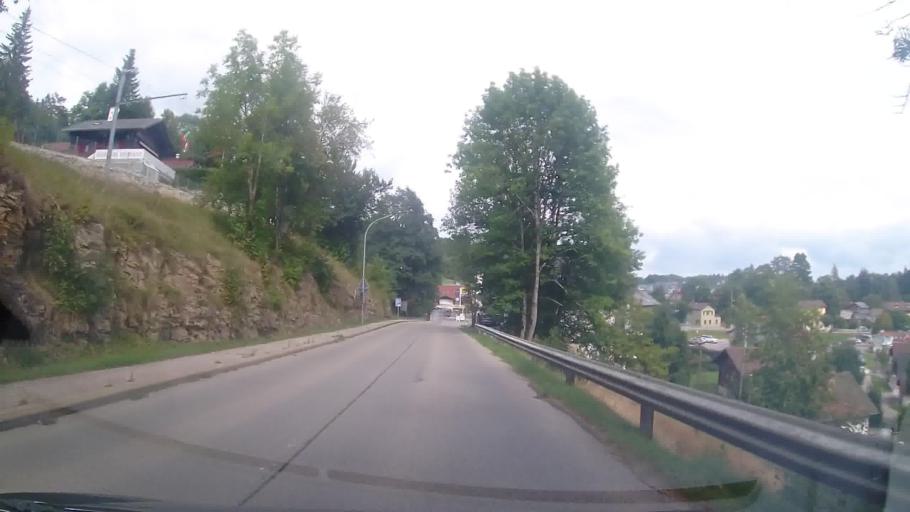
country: CH
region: Vaud
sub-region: Nyon District
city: Saint-Cergue
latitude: 46.4466
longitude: 6.1545
